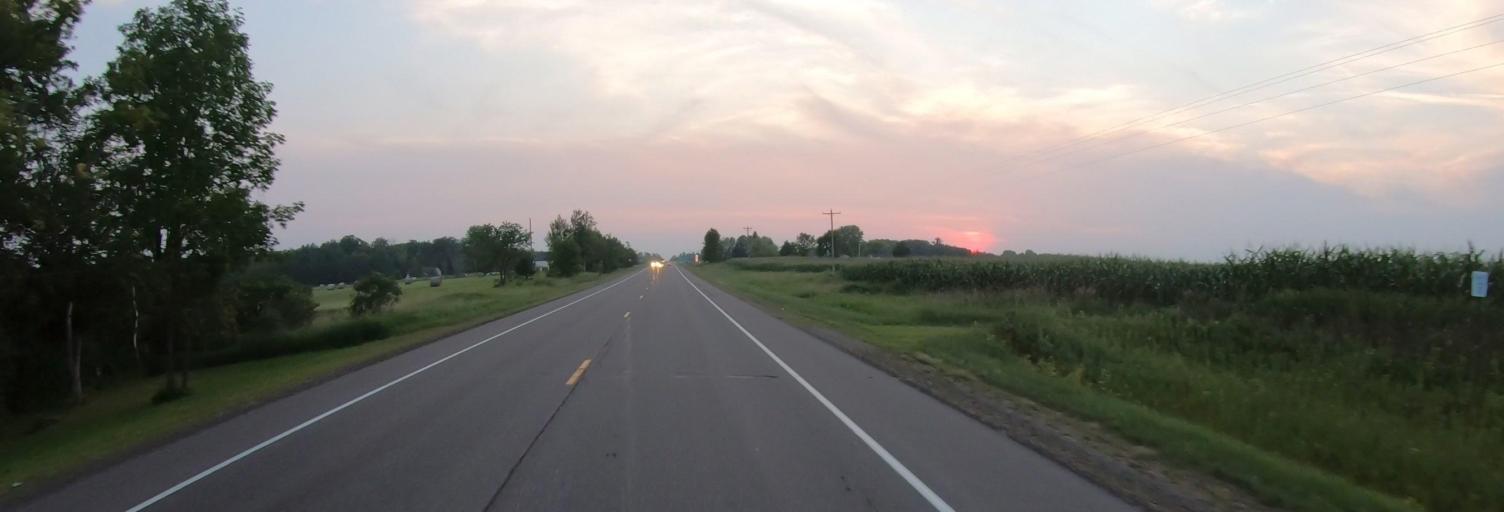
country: US
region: Minnesota
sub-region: Pine County
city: Rock Creek
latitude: 45.7666
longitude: -92.9786
